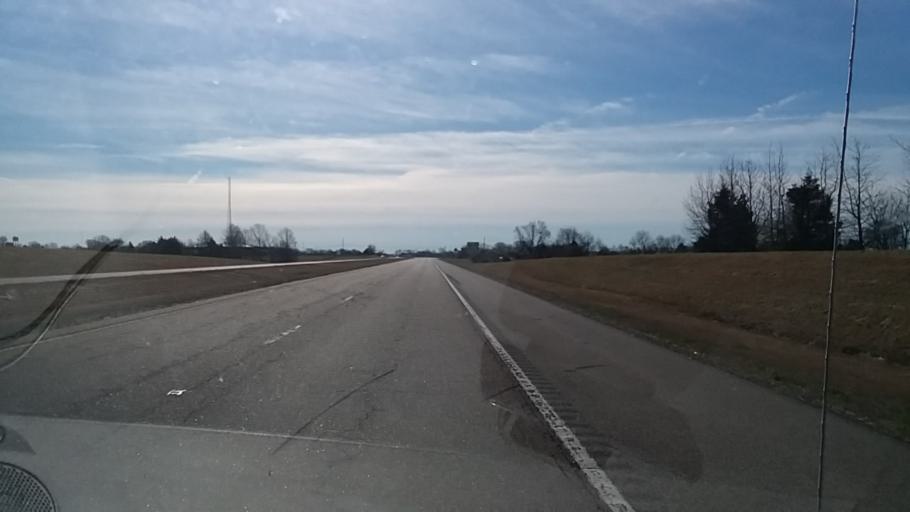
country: US
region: Tennessee
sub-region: Crockett County
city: Alamo
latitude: 35.7857
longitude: -89.1484
